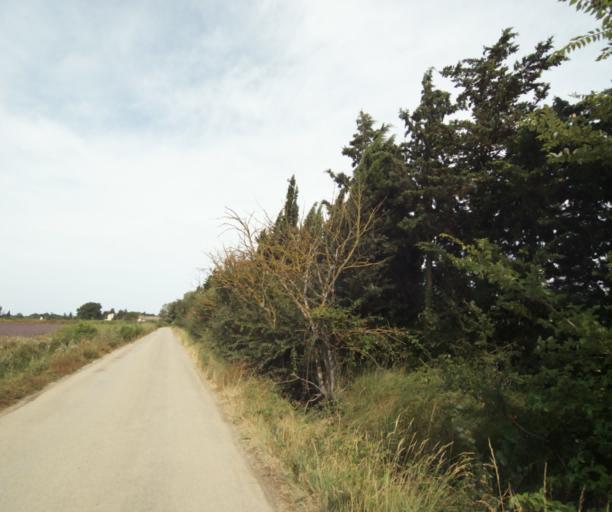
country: FR
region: Languedoc-Roussillon
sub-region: Departement de l'Herault
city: Marsillargues
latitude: 43.6320
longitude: 4.1789
